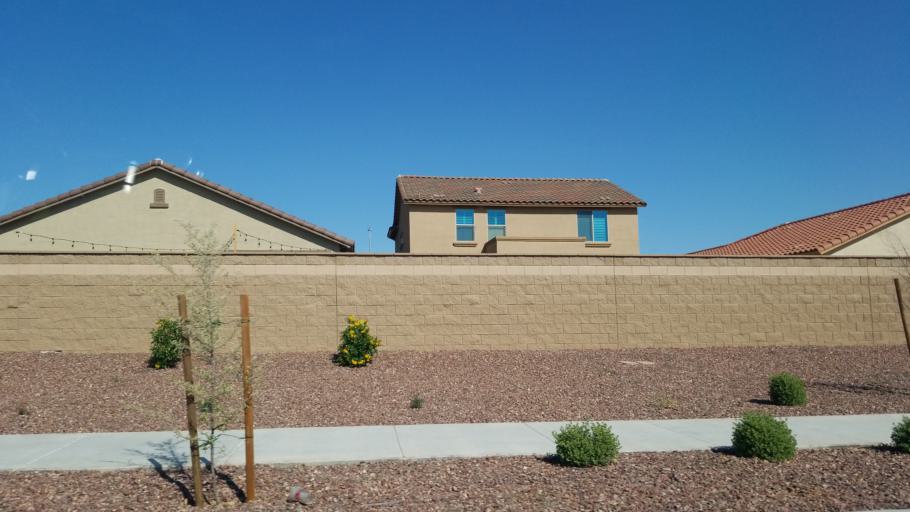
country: US
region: Arizona
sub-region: Maricopa County
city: Glendale
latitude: 33.5607
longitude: -112.1949
